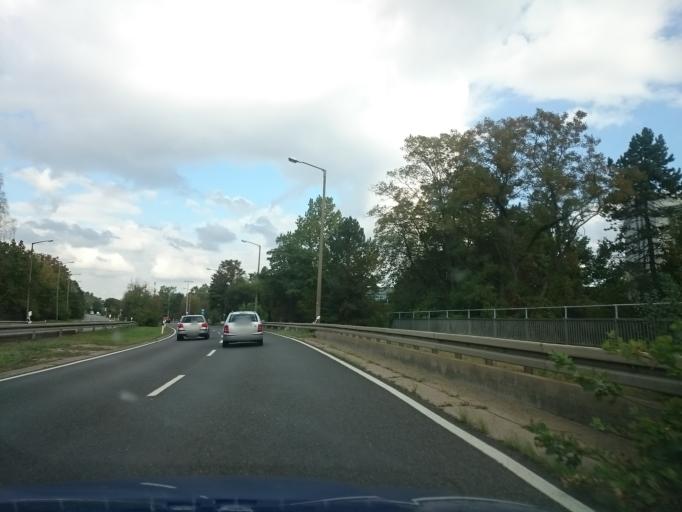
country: DE
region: Bavaria
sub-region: Regierungsbezirk Mittelfranken
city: Nuernberg
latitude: 49.4154
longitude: 11.1122
